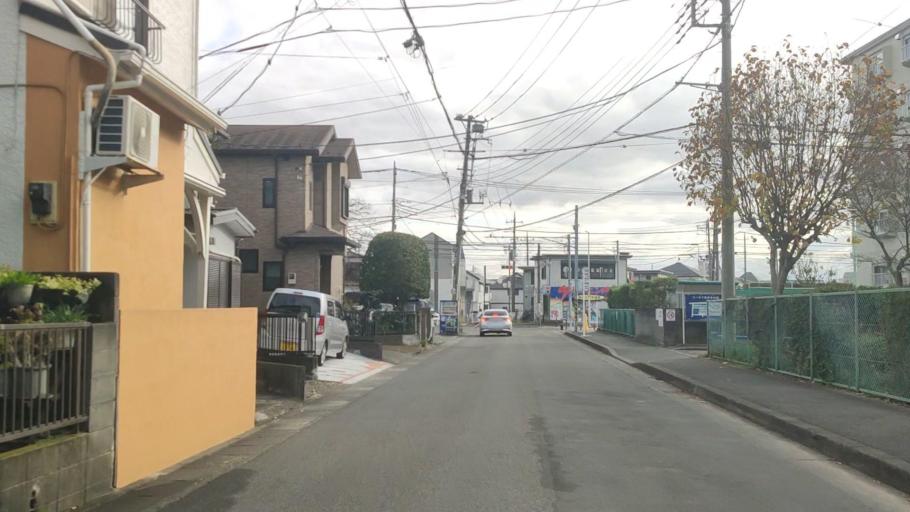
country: JP
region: Kanagawa
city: Minami-rinkan
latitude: 35.4877
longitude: 139.4468
